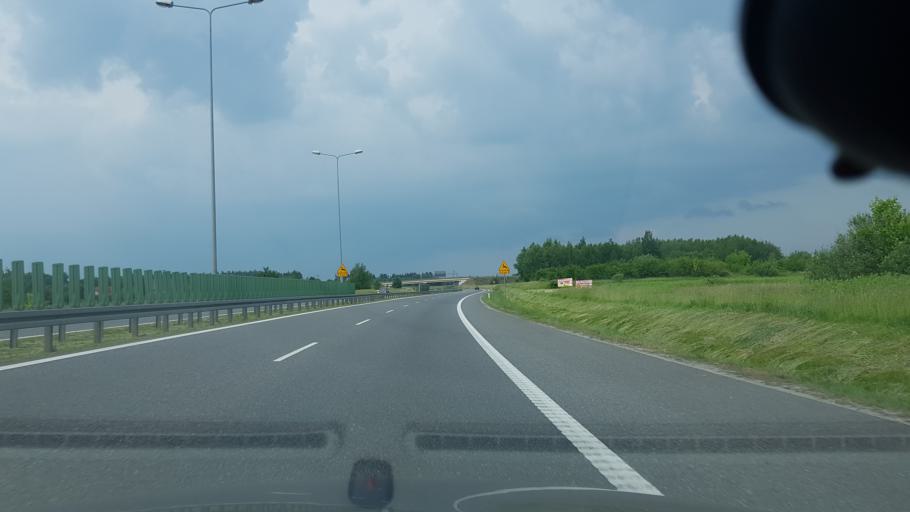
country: PL
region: Masovian Voivodeship
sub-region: Powiat legionowski
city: Serock
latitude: 52.5129
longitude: 21.0506
